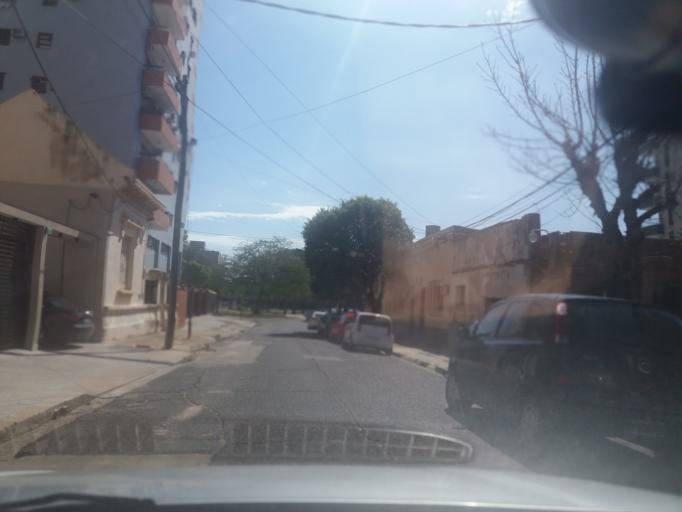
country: AR
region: Corrientes
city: Corrientes
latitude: -27.4663
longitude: -58.8454
